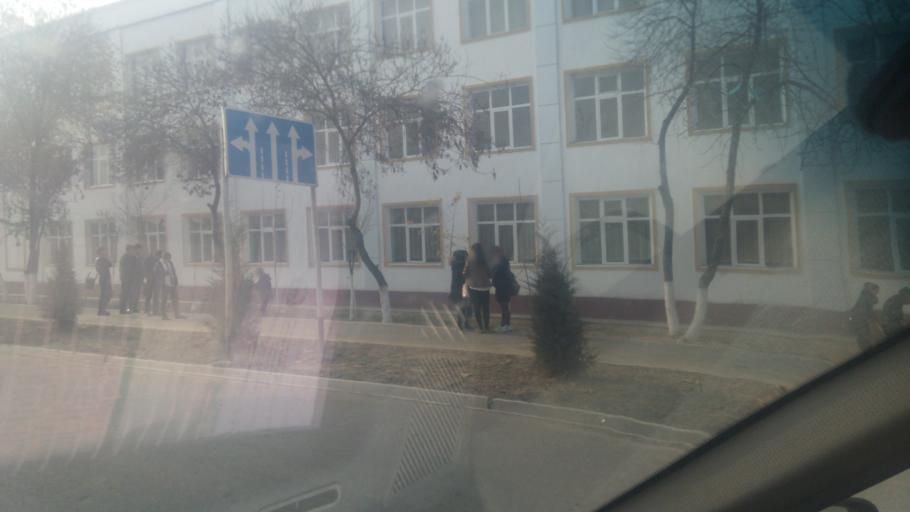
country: UZ
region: Sirdaryo
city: Guliston
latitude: 40.5110
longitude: 68.7707
